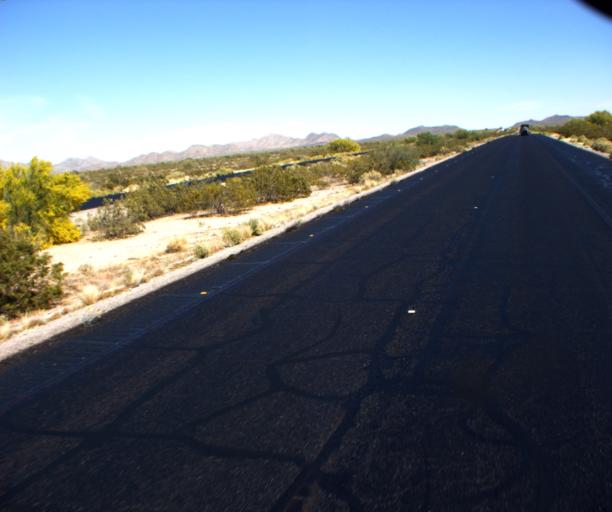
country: US
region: Arizona
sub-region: Pinal County
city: Maricopa
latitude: 32.8404
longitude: -112.2420
